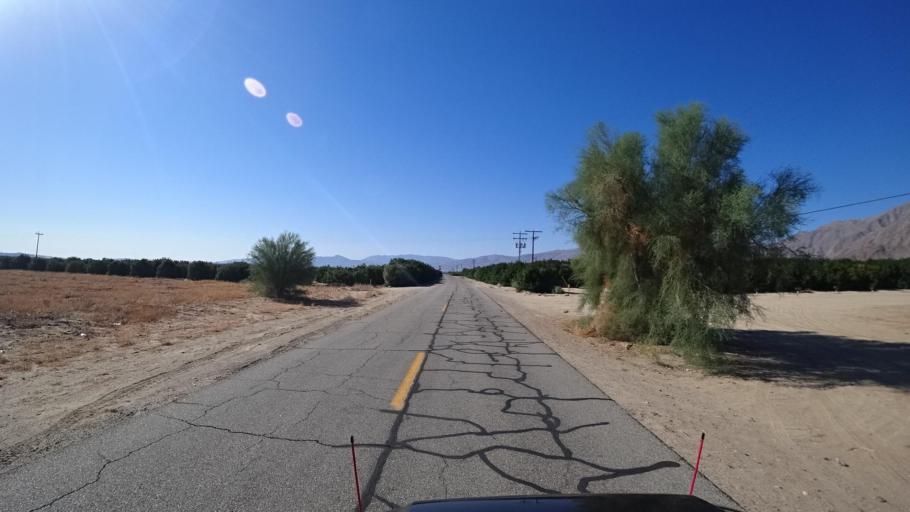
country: US
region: California
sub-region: San Diego County
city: Borrego Springs
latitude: 33.3120
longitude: -116.3676
